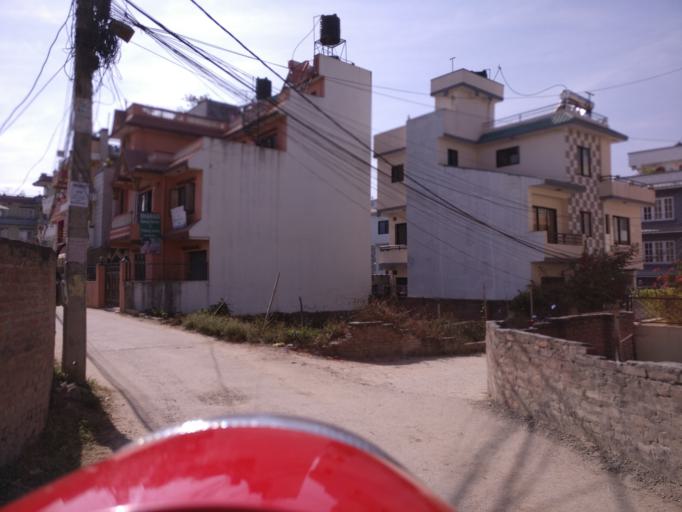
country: NP
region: Central Region
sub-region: Bagmati Zone
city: Patan
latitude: 27.6602
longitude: 85.3093
